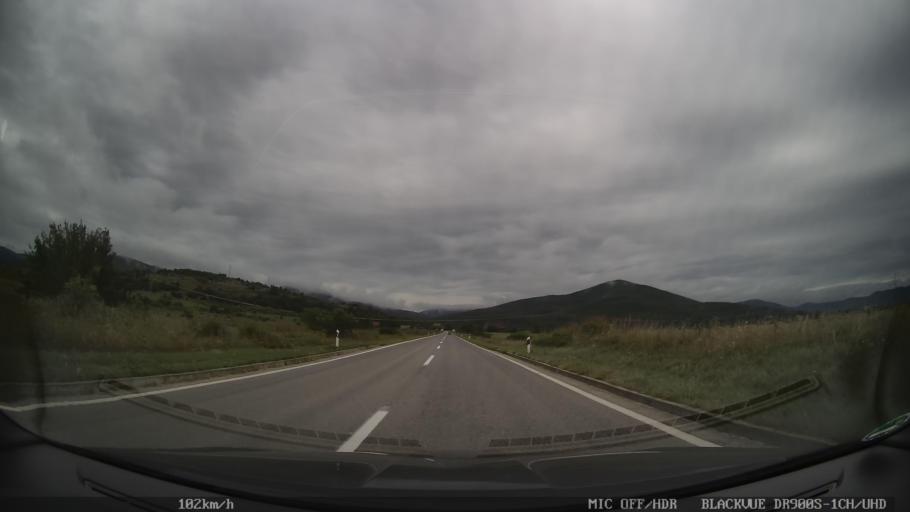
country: HR
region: Licko-Senjska
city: Otocac
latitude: 44.8583
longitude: 15.3183
